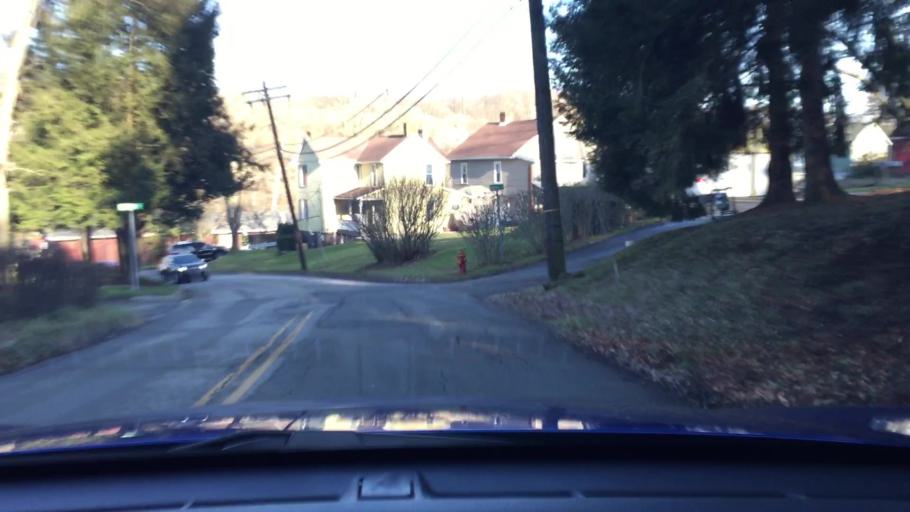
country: US
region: Pennsylvania
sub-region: Westmoreland County
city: Murrysville
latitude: 40.4198
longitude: -79.6361
